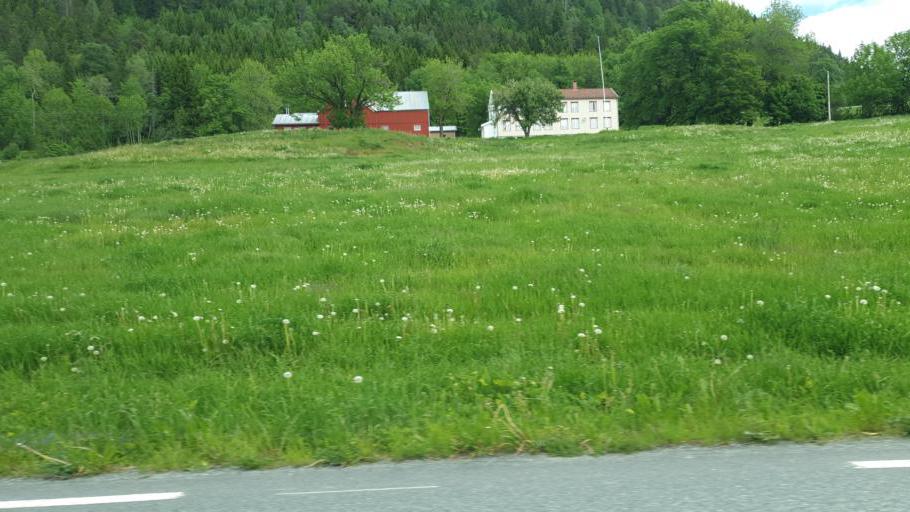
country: NO
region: Sor-Trondelag
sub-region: Trondheim
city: Trondheim
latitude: 63.5570
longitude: 10.3008
